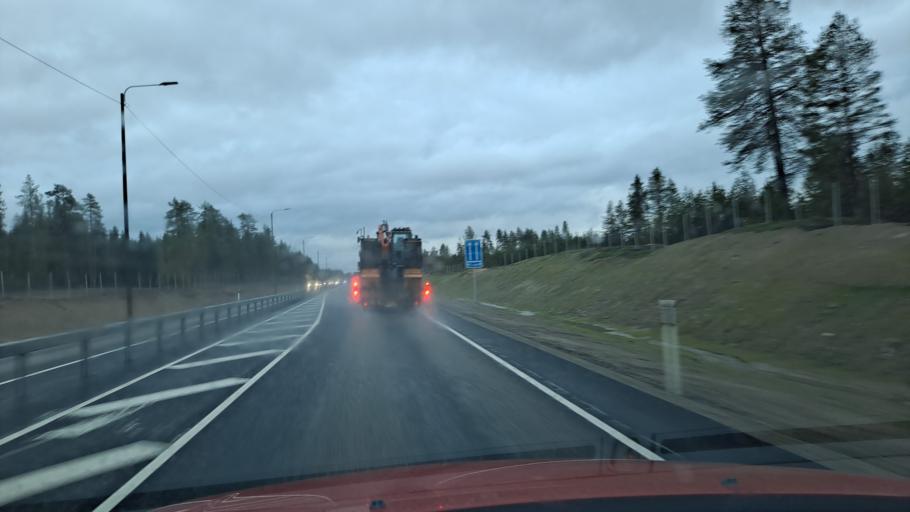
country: FI
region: Lapland
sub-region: Kemi-Tornio
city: Simo
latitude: 65.6539
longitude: 25.0897
